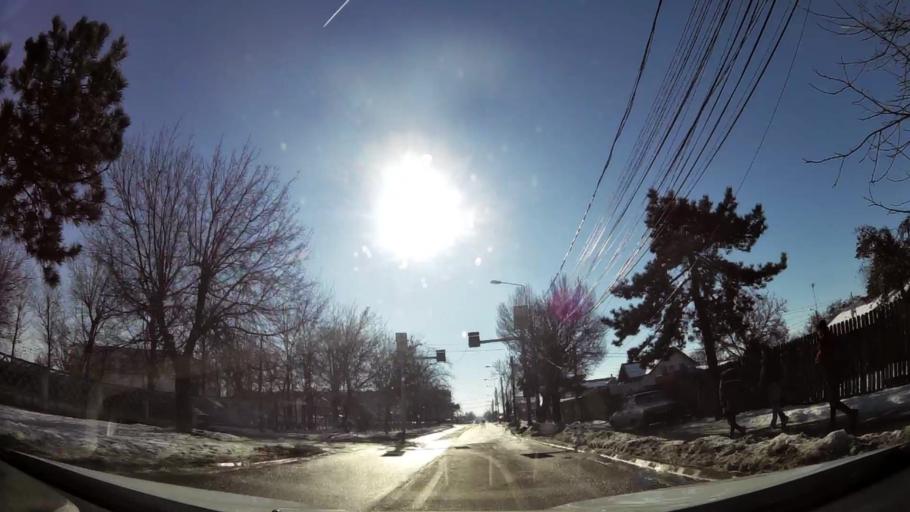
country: RO
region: Ilfov
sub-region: Comuna Magurele
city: Magurele
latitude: 44.3889
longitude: 26.0474
